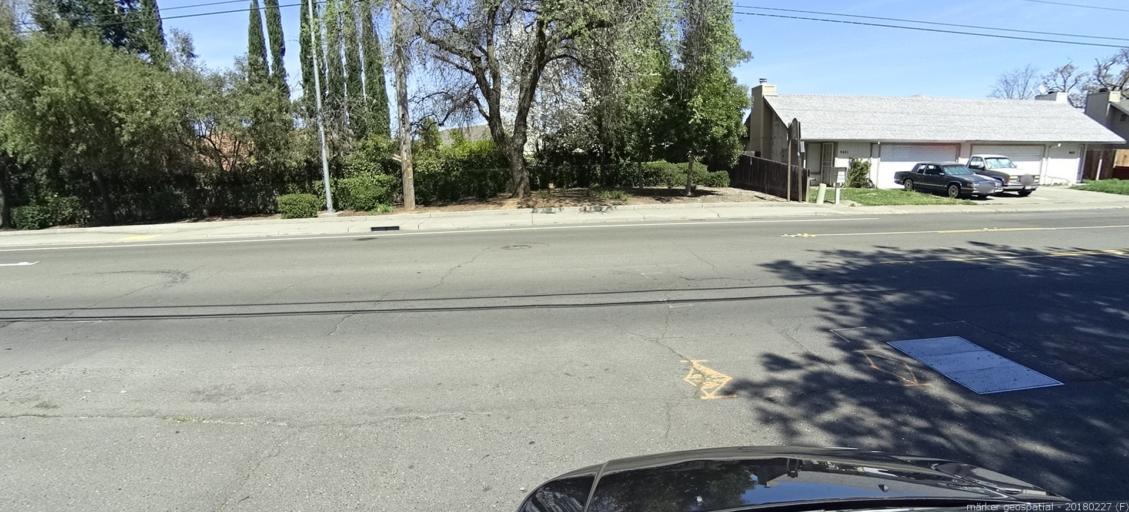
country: US
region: California
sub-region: Sacramento County
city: La Riviera
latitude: 38.5546
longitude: -121.3398
